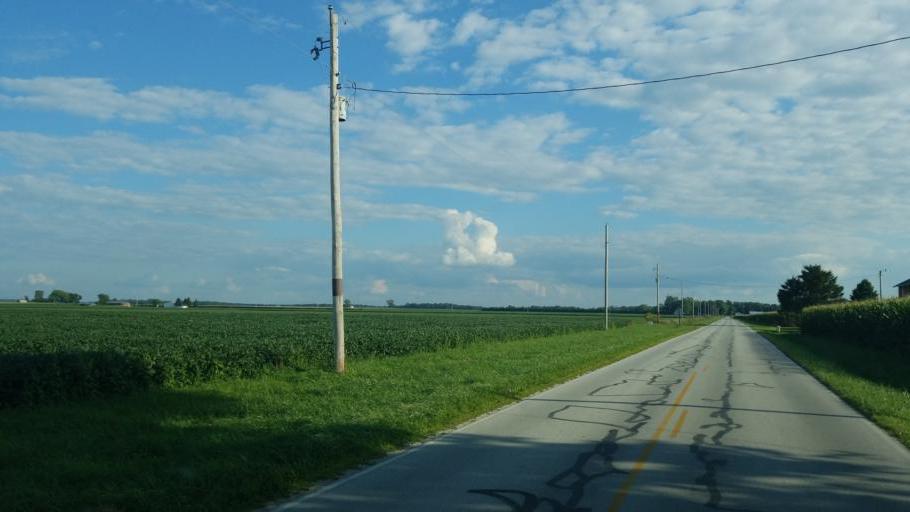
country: US
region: Ohio
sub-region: Sandusky County
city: Green Springs
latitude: 41.2392
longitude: -83.1311
